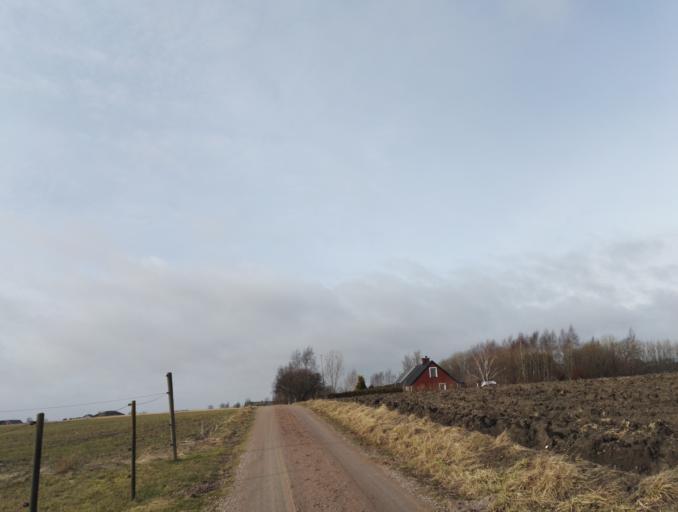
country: SE
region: Skane
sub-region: Landskrona
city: Asmundtorp
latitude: 55.8932
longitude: 13.0029
